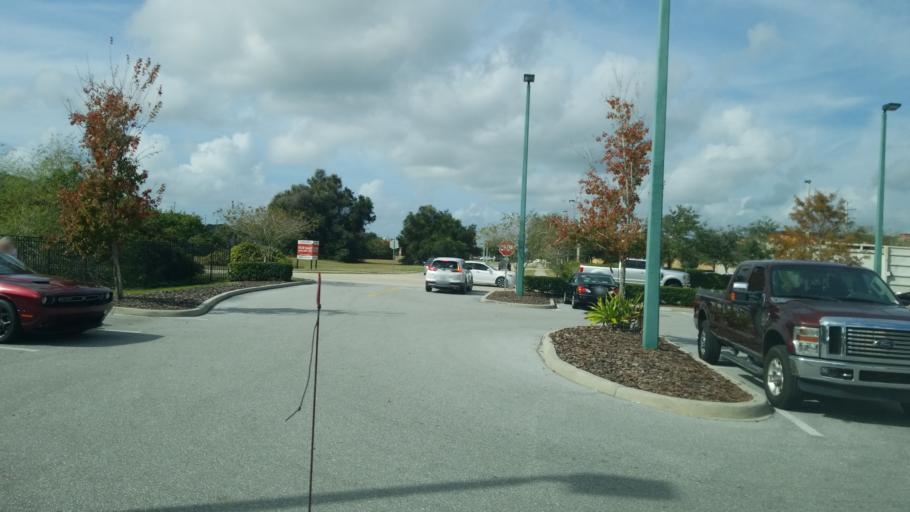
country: US
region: Florida
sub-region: Sarasota County
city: North Port
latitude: 27.0332
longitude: -82.2081
